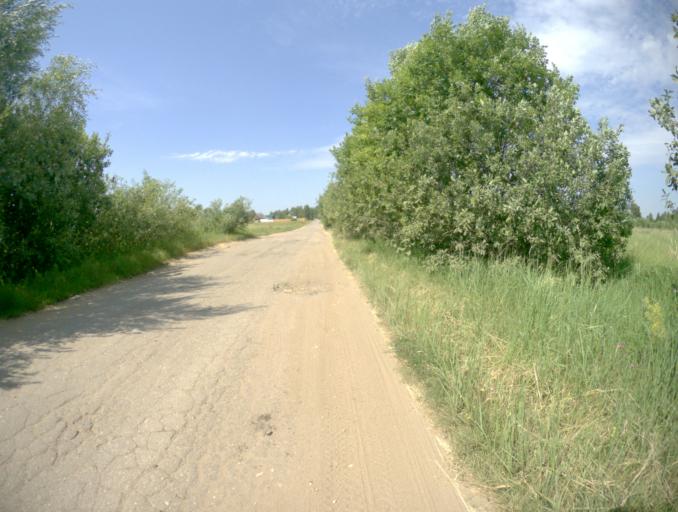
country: RU
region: Vladimir
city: Vorsha
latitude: 56.0248
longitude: 40.1852
